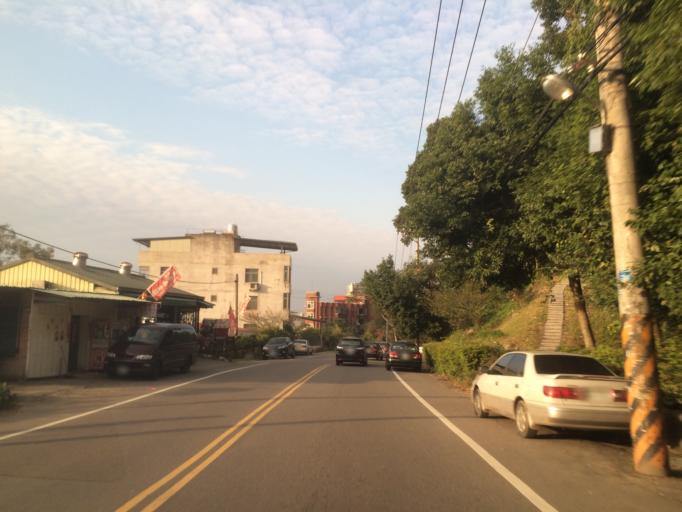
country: TW
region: Taiwan
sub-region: Hsinchu
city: Zhubei
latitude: 24.7136
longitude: 121.0977
